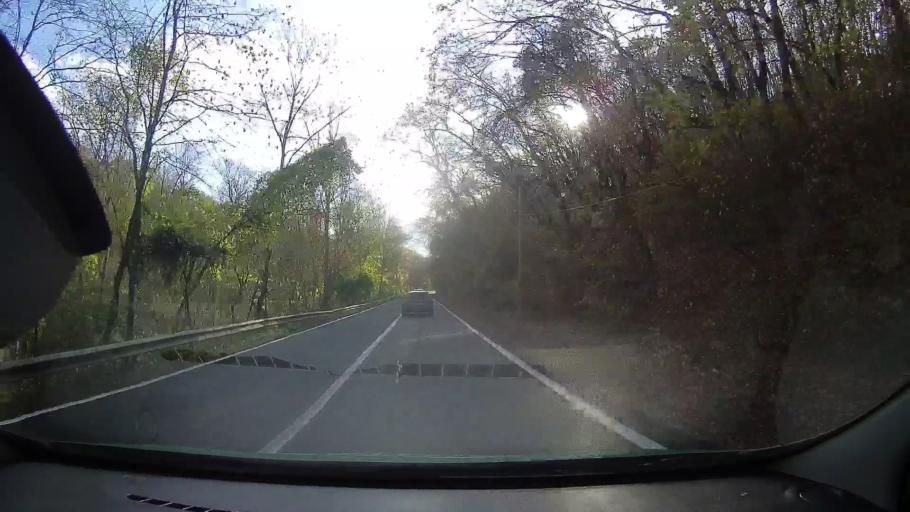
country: RO
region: Tulcea
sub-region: Comuna Topolog
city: Topolog
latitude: 44.9168
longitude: 28.4213
